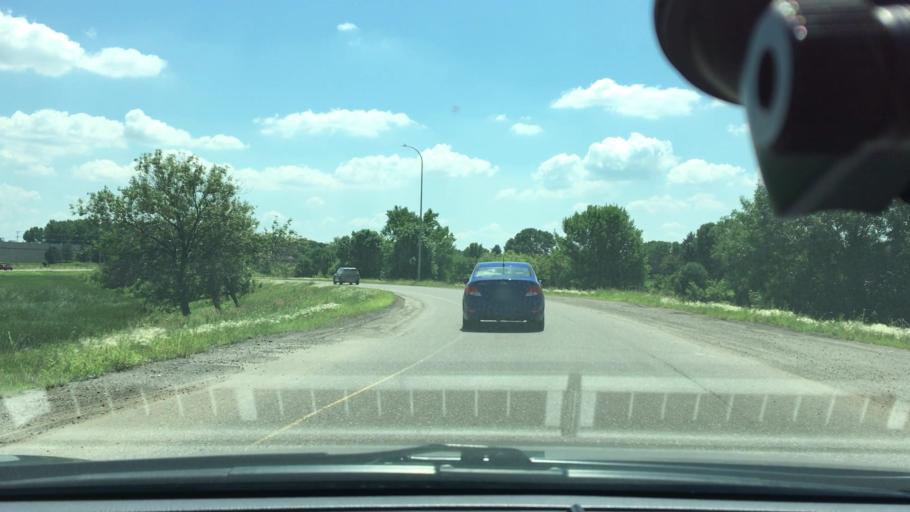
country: US
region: Minnesota
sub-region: Hennepin County
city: Osseo
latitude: 45.0943
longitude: -93.4045
